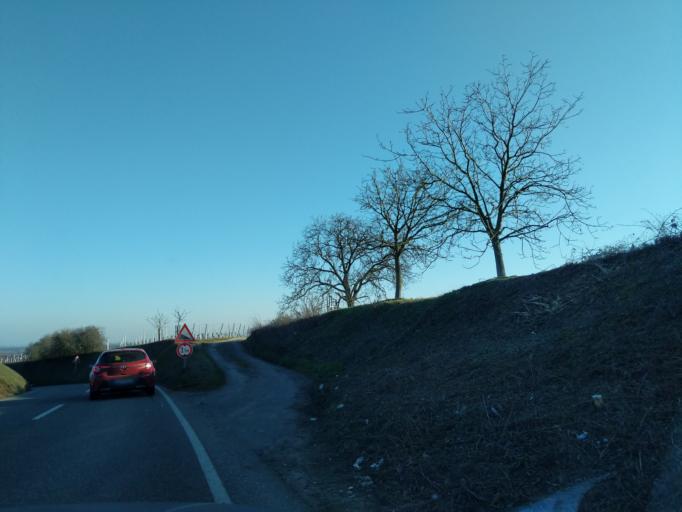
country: DE
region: Rheinland-Pfalz
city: Dackenheim
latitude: 49.5198
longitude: 8.1888
